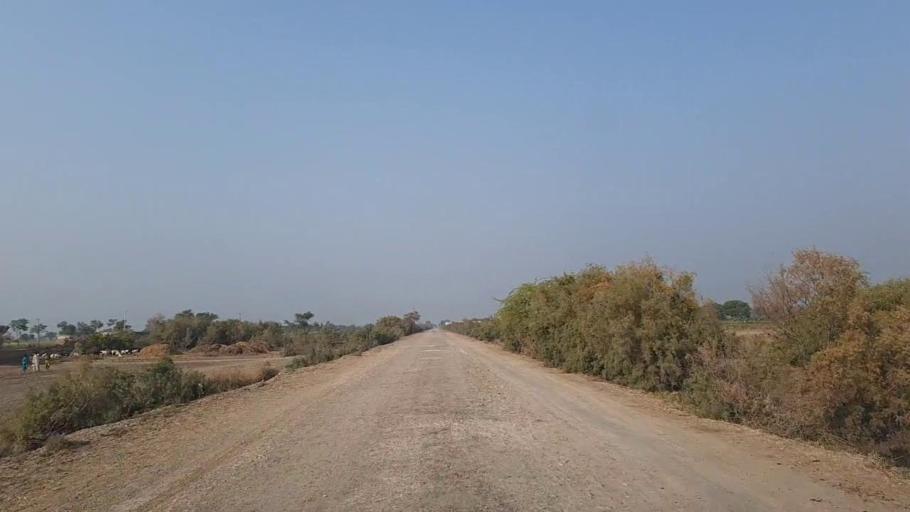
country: PK
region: Sindh
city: Nawabshah
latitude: 26.3347
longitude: 68.4891
